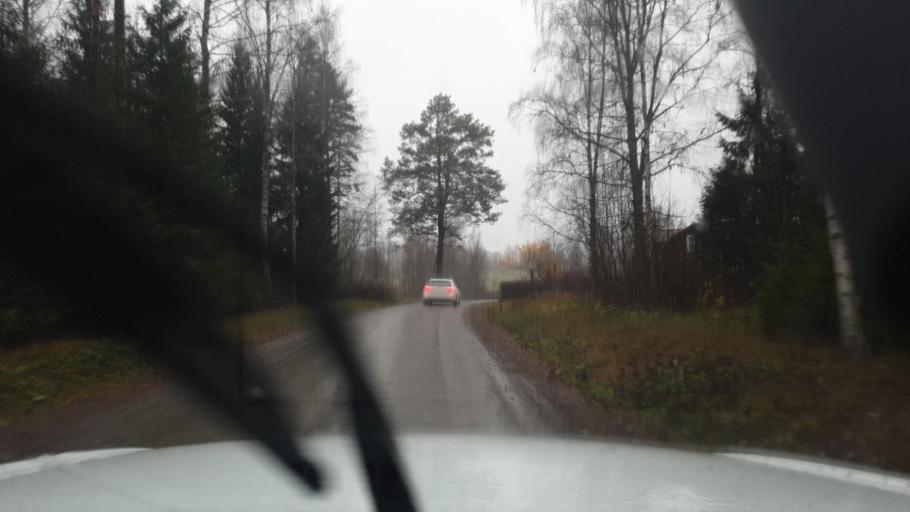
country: SE
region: Vaermland
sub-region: Sunne Kommun
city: Sunne
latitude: 59.8105
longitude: 13.0650
